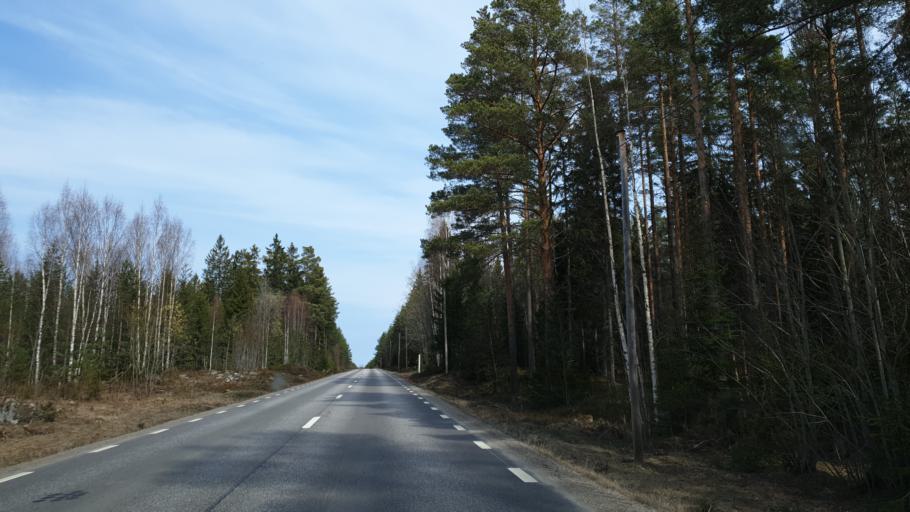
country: SE
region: Gaevleborg
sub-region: Gavle Kommun
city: Norrsundet
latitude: 61.0063
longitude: 17.1295
